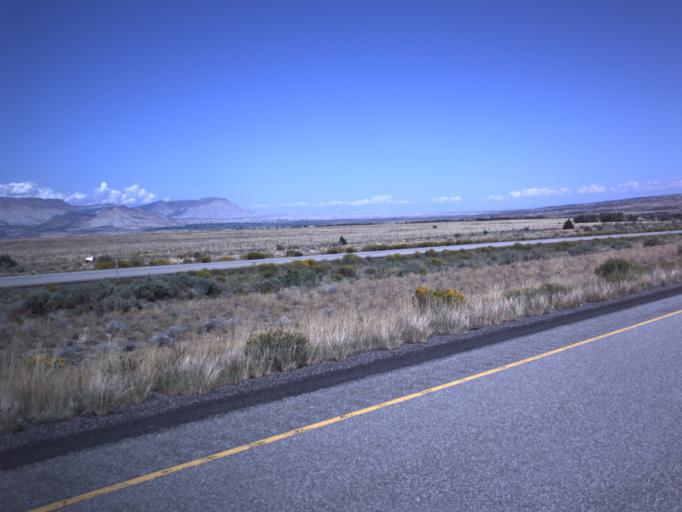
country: US
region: Utah
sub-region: Emery County
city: Ferron
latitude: 38.7783
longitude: -111.3157
